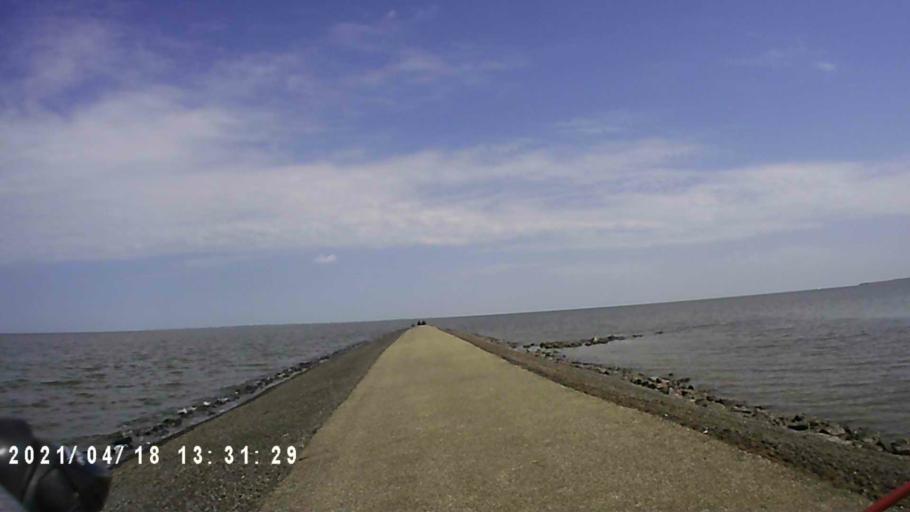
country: NL
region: Friesland
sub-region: Gemeente Dongeradeel
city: Anjum
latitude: 53.4138
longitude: 6.0985
